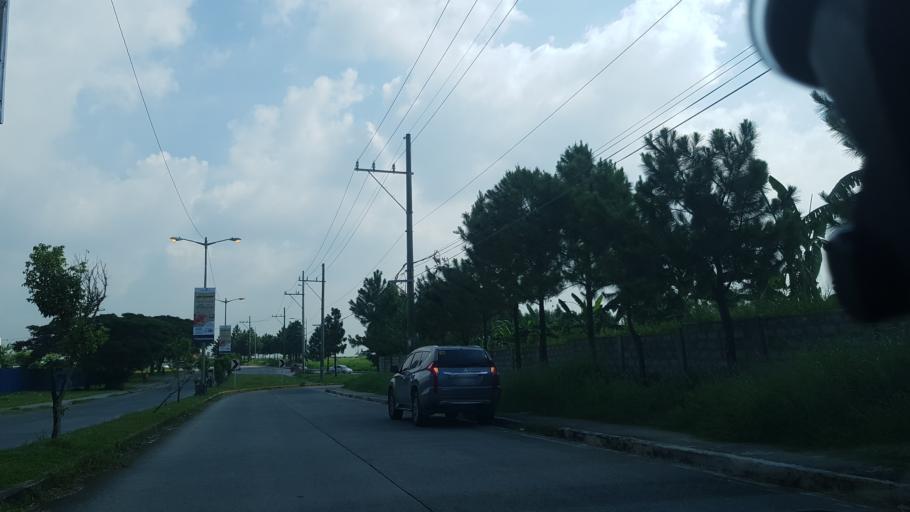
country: PH
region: Calabarzon
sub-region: Province of Laguna
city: San Pedro
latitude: 14.3725
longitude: 121.0116
